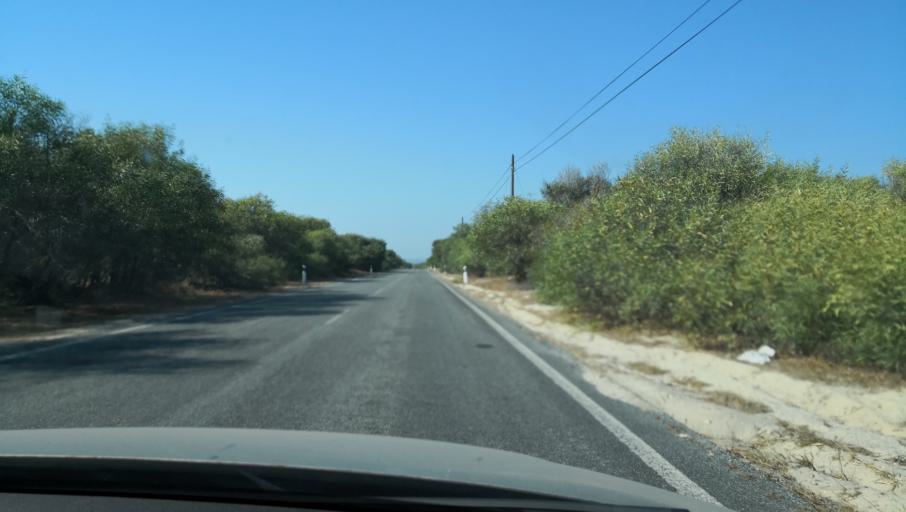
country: PT
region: Setubal
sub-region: Setubal
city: Setubal
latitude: 38.4038
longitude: -8.8082
